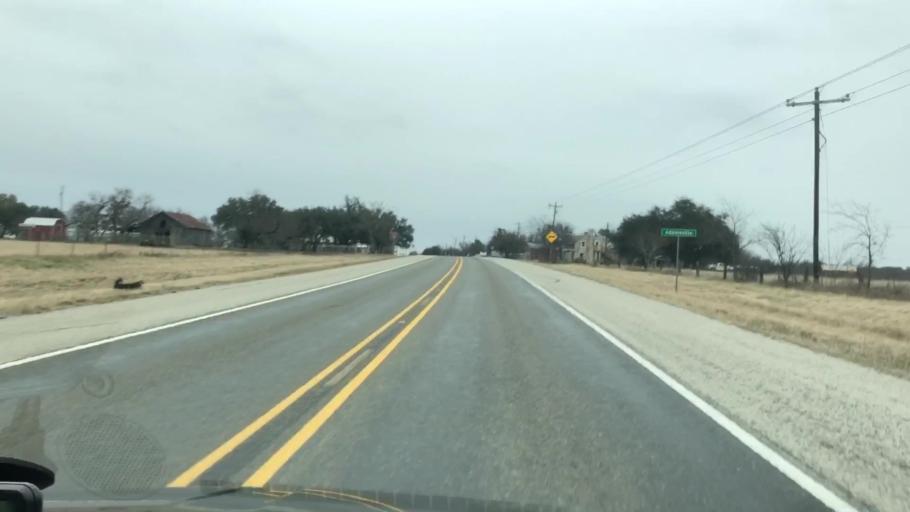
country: US
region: Texas
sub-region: Lampasas County
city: Lampasas
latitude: 31.2983
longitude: -98.1688
